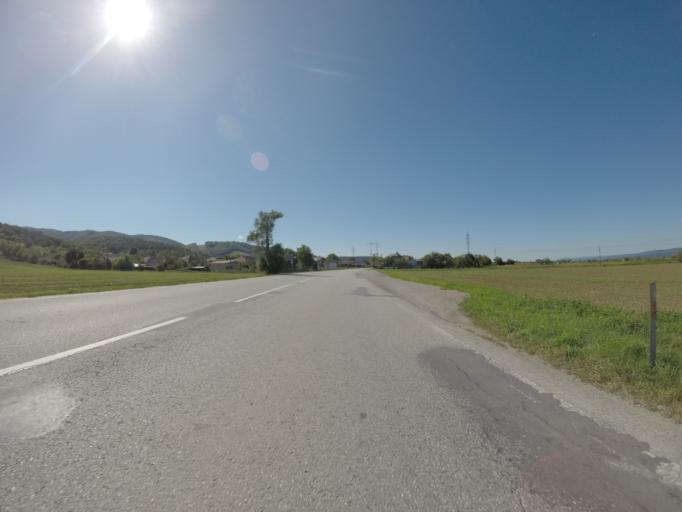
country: SK
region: Nitriansky
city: Ilava
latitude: 49.0186
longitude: 18.2769
